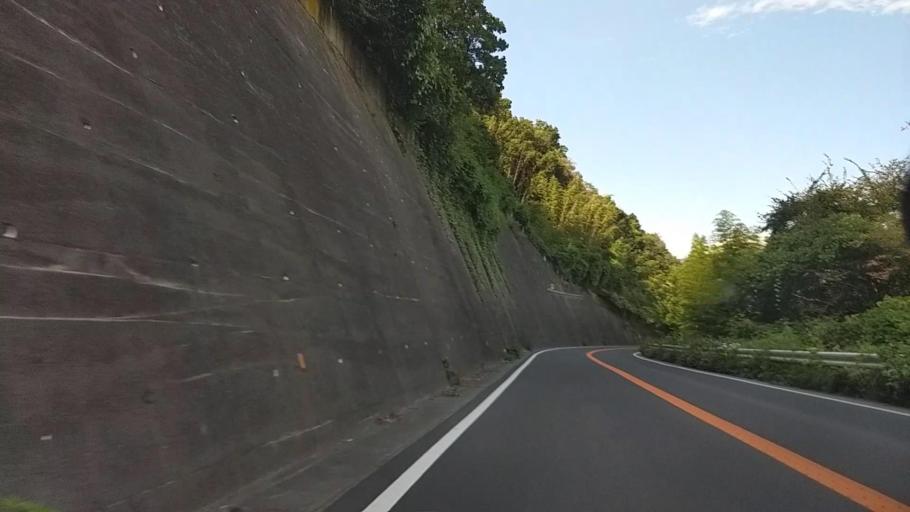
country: JP
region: Shizuoka
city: Fujinomiya
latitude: 35.3976
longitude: 138.4415
